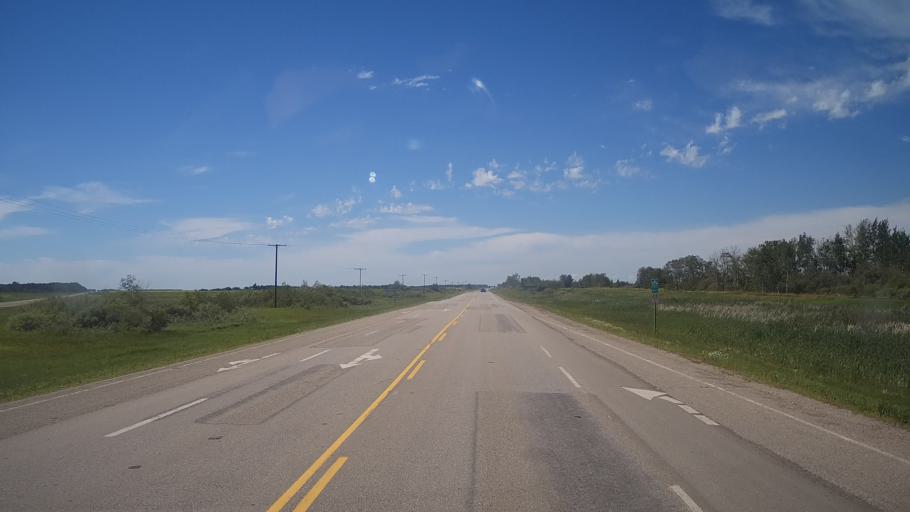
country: CA
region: Saskatchewan
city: Langenburg
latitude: 50.8011
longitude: -101.5791
